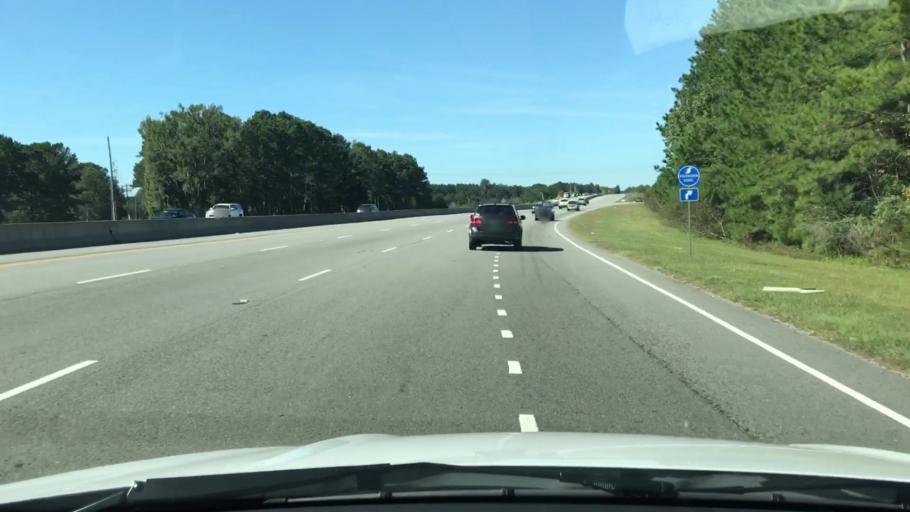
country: US
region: South Carolina
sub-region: Beaufort County
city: Bluffton
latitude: 32.2901
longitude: -80.9322
